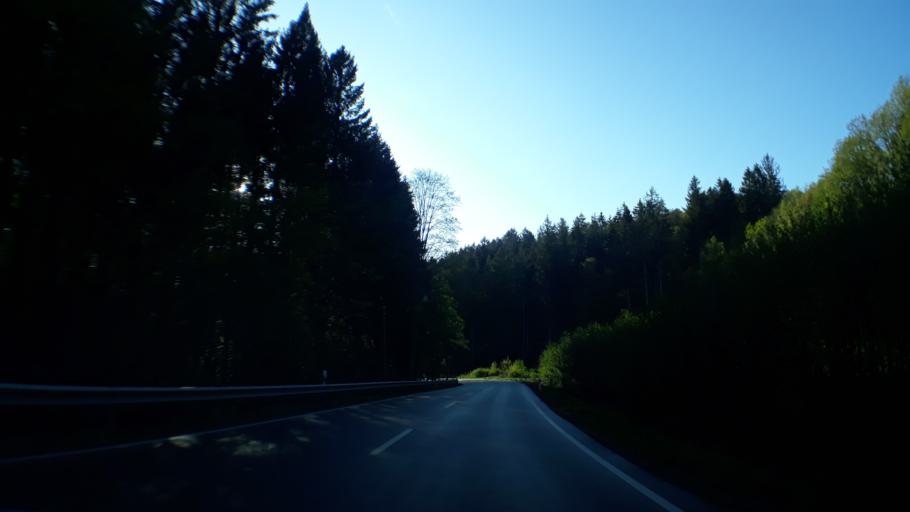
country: DE
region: North Rhine-Westphalia
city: Stolberg
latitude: 50.7092
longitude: 6.2804
